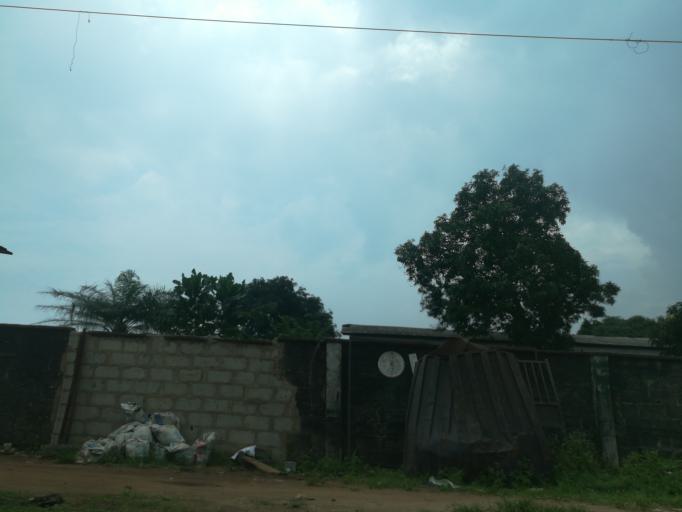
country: NG
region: Lagos
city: Ikorodu
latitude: 6.5778
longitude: 3.5908
